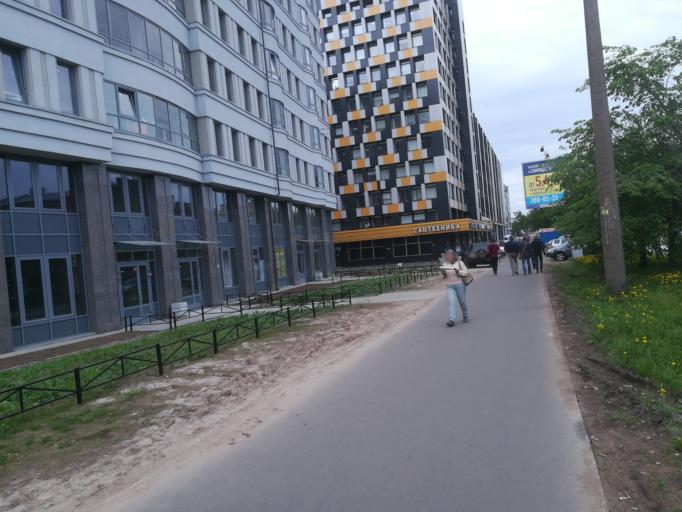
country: RU
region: St.-Petersburg
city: Vasyl'evsky Ostrov
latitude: 59.9490
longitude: 30.2680
